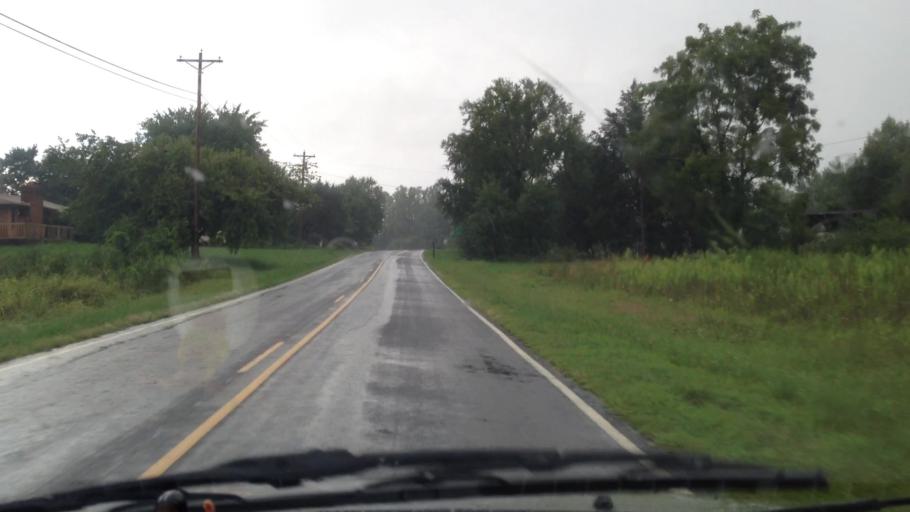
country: US
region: North Carolina
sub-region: Guilford County
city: Stokesdale
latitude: 36.2161
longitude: -80.0294
